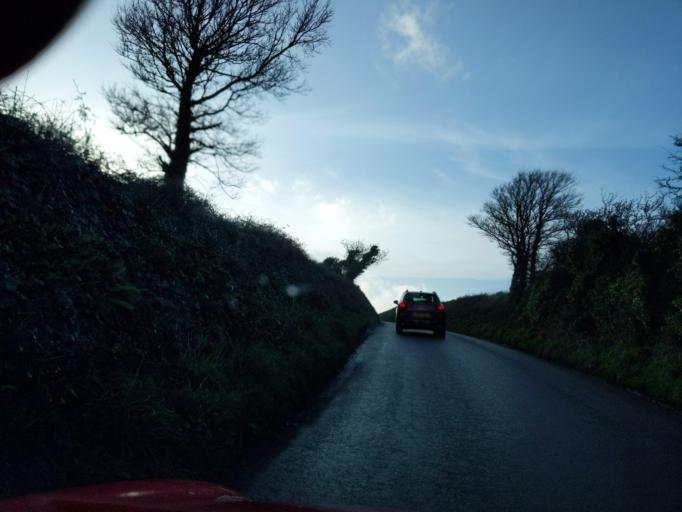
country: GB
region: England
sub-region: Cornwall
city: Fowey
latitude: 50.3348
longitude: -4.5931
